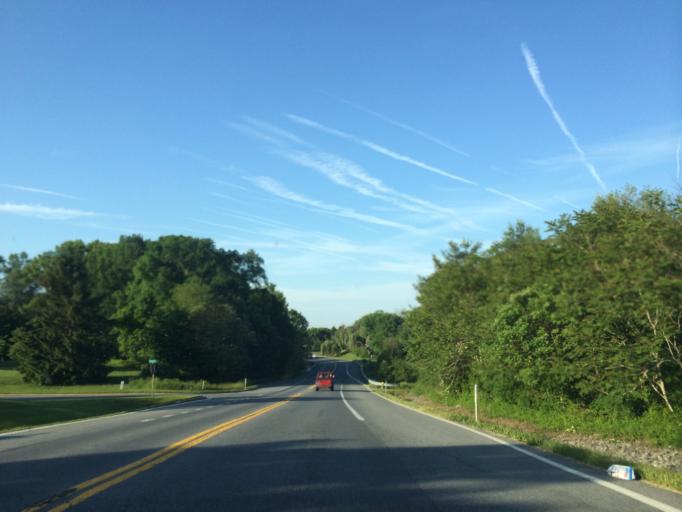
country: US
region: Maryland
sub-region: Carroll County
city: Sykesville
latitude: 39.3972
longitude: -77.0174
